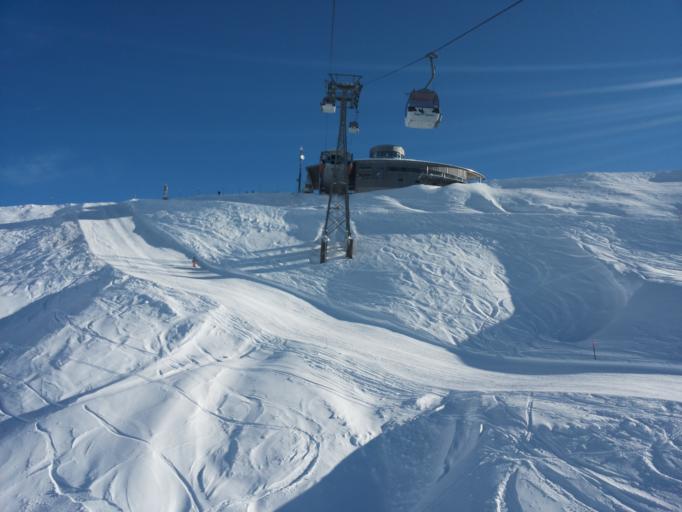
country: CH
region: Bern
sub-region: Interlaken-Oberhasli District
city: Meiringen
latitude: 46.7387
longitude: 8.2556
